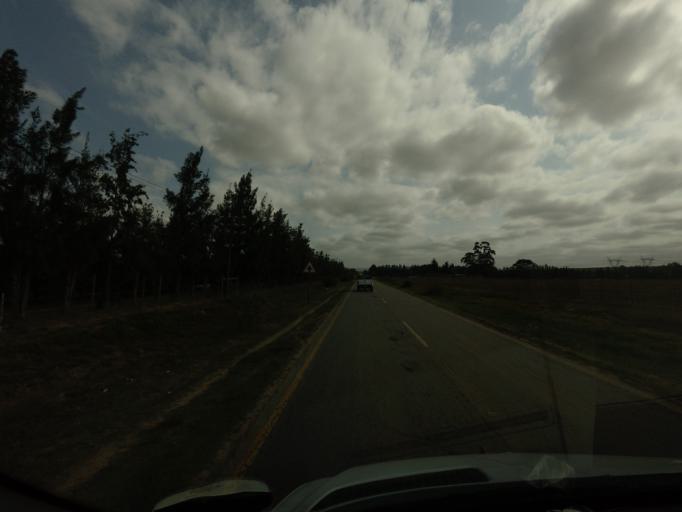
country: ZA
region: Eastern Cape
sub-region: Cacadu District Municipality
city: Kirkwood
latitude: -33.5174
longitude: 25.6925
